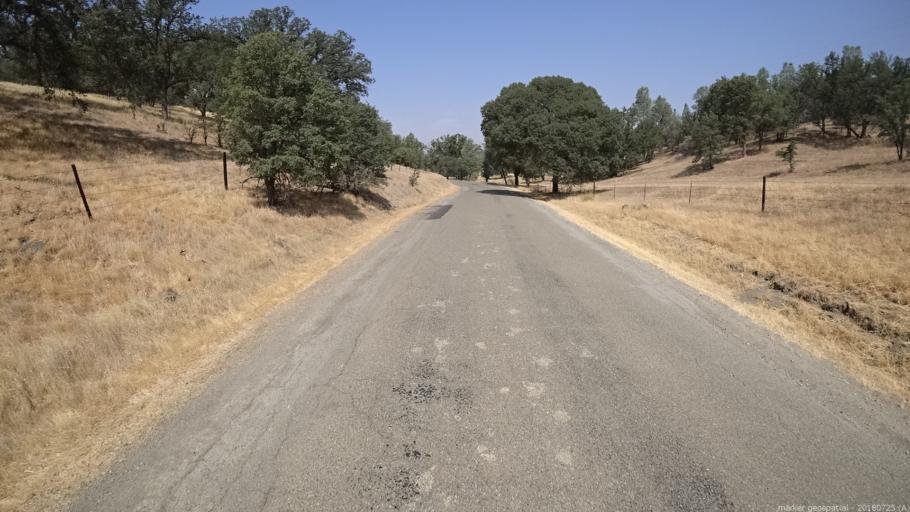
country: US
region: California
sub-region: San Luis Obispo County
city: Shandon
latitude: 35.8675
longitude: -120.4021
